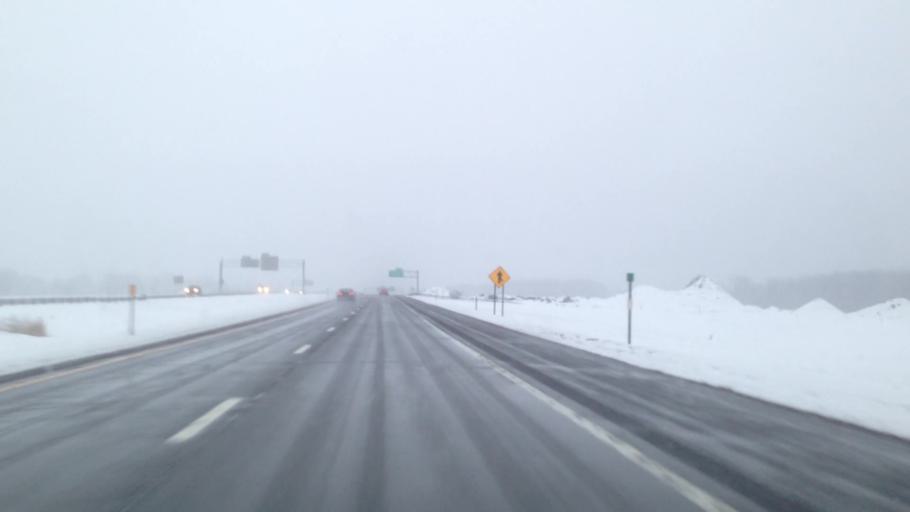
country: US
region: New York
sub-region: Onondaga County
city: East Syracuse
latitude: 43.0743
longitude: -76.0533
